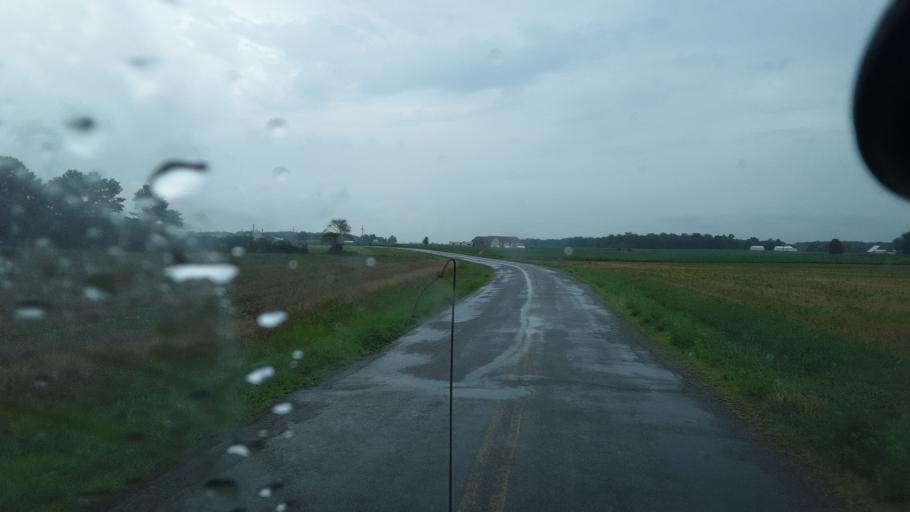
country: US
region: Ohio
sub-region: Williams County
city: Edgerton
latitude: 41.5241
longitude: -84.7999
